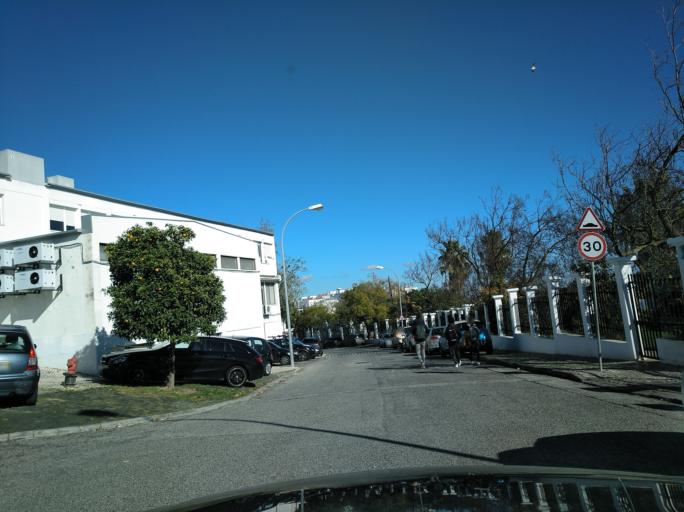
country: PT
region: Lisbon
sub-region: Loures
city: Moscavide
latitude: 38.7442
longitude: -9.1079
